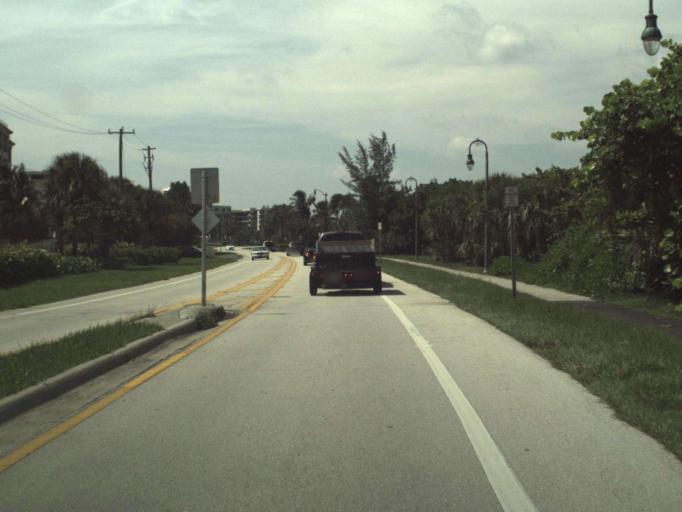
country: US
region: Florida
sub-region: Palm Beach County
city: Lake Worth
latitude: 26.6129
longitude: -80.0387
